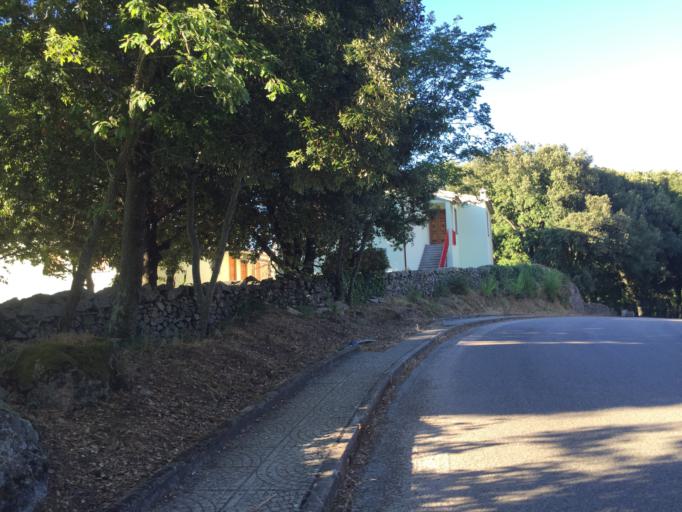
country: IT
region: Sardinia
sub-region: Provincia di Olbia-Tempio
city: Aggius
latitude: 40.9332
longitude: 9.0660
